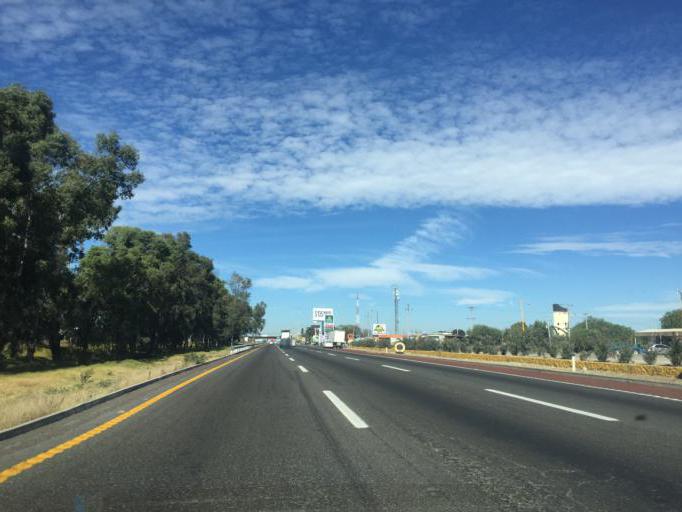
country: MX
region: Queretaro
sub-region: San Juan del Rio
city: Paso de Mata
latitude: 20.2932
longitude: -99.9236
